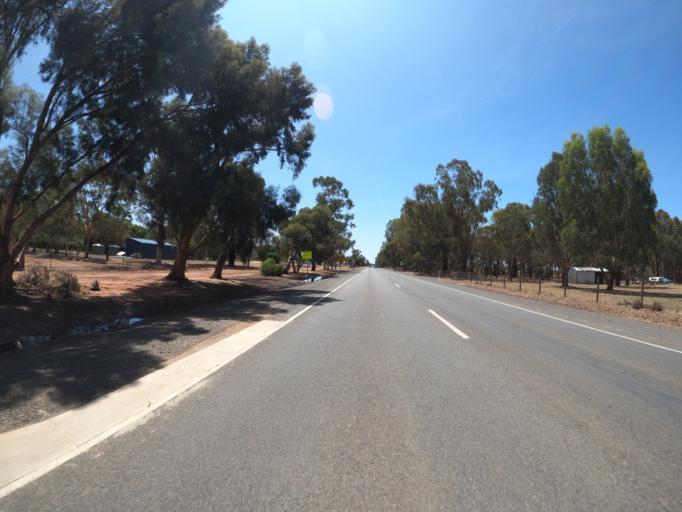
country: AU
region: Victoria
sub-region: Moira
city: Yarrawonga
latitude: -36.0373
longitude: 145.9955
